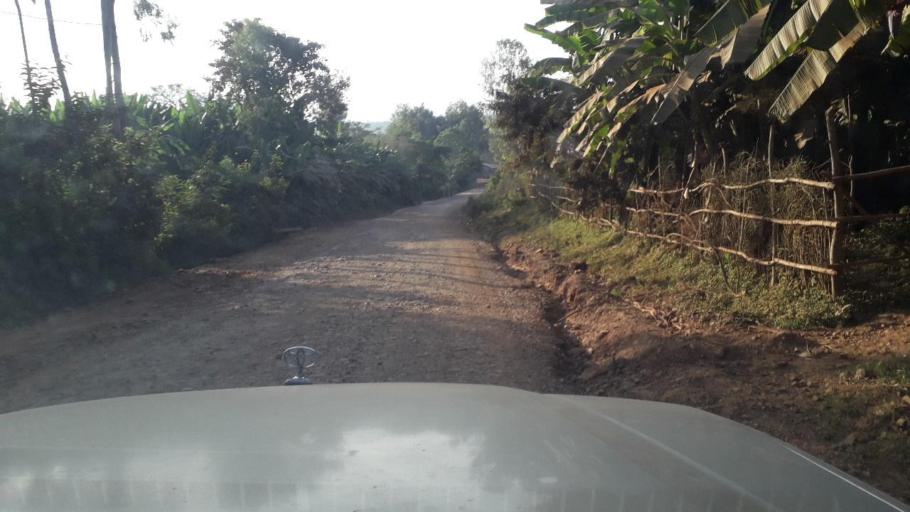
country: ET
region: Oromiya
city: Jima
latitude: 7.6061
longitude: 36.8399
